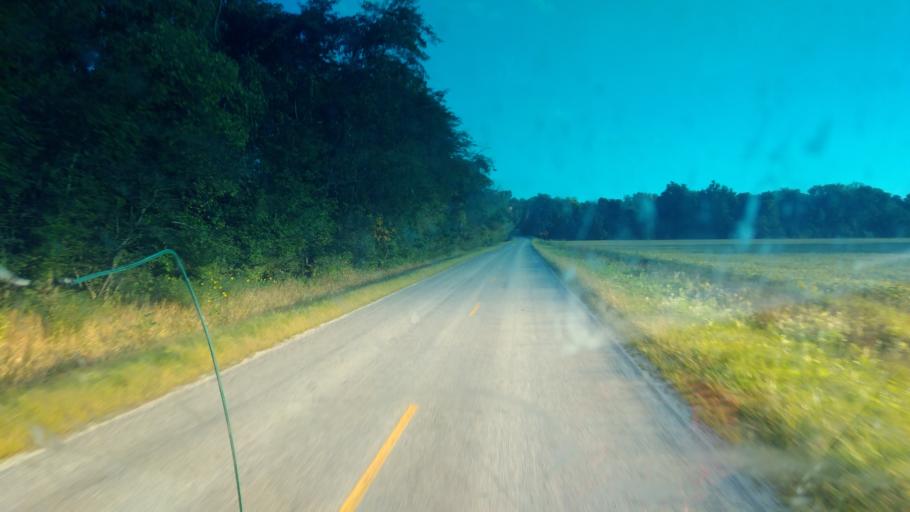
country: US
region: Ohio
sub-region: Crawford County
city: Bucyrus
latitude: 40.8389
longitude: -82.8731
